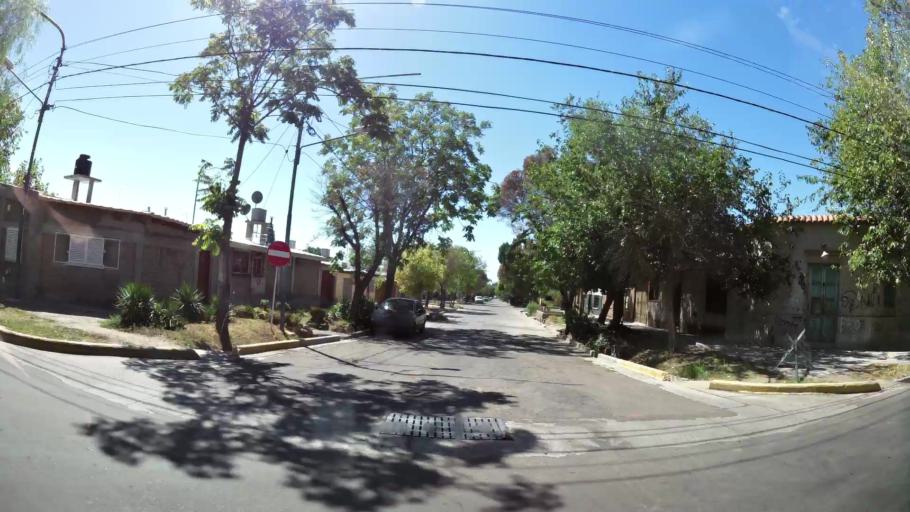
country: AR
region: Mendoza
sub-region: Departamento de Godoy Cruz
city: Godoy Cruz
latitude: -32.9058
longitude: -68.8653
